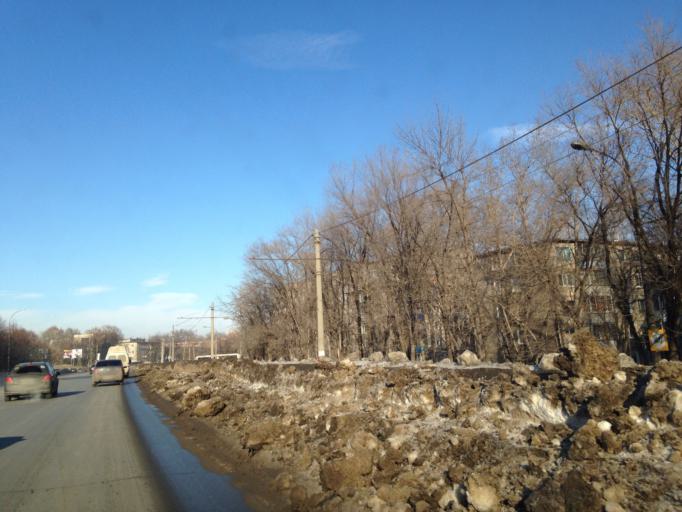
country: RU
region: Ulyanovsk
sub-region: Ulyanovskiy Rayon
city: Ulyanovsk
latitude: 54.3084
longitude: 48.3501
